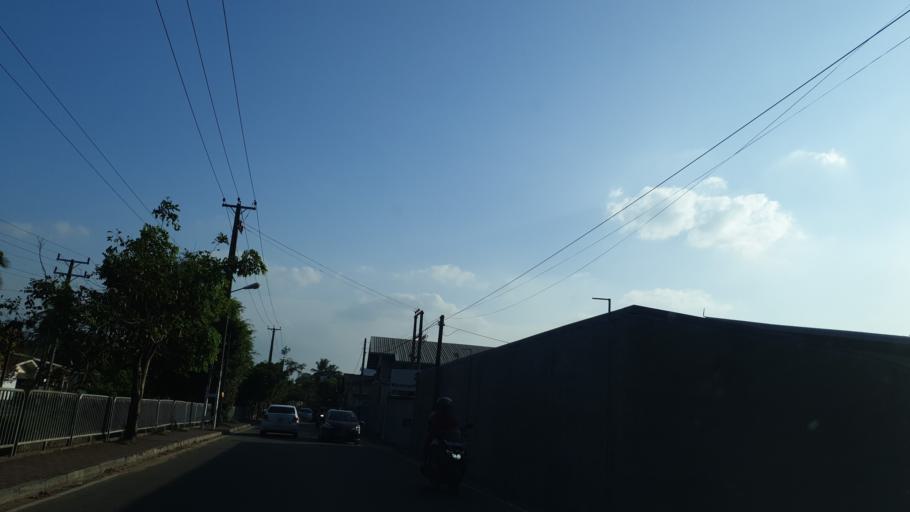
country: LK
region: Western
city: Galkissa
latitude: 6.8484
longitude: 79.8771
